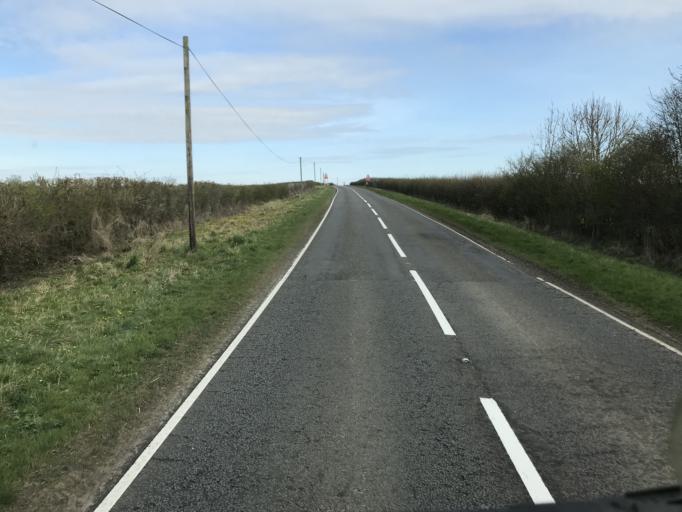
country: GB
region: England
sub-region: Lincolnshire
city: Market Rasen
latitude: 53.3918
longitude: -0.4054
